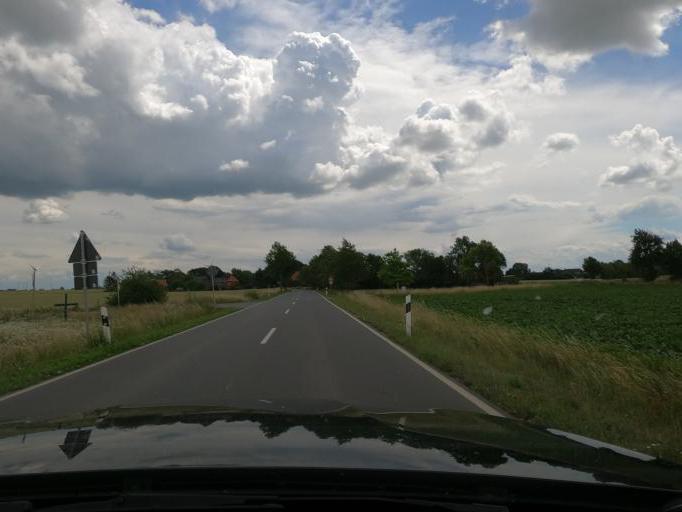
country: DE
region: Lower Saxony
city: Sehnde
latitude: 52.2888
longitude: 10.0103
